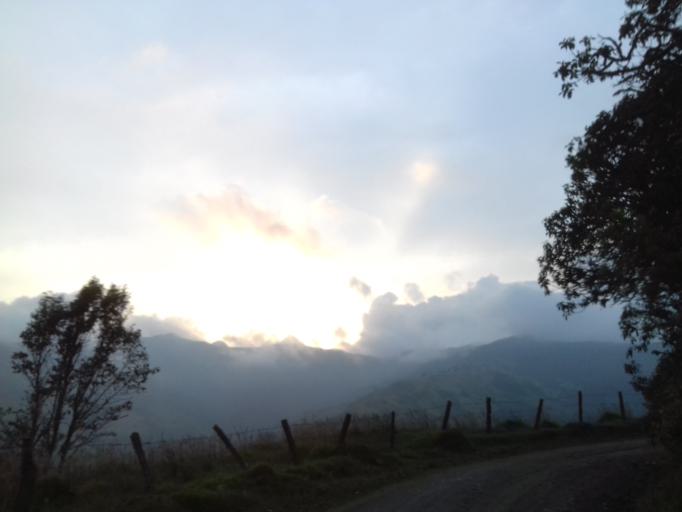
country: CO
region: Quindio
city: Salento
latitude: 4.5481
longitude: -75.4941
